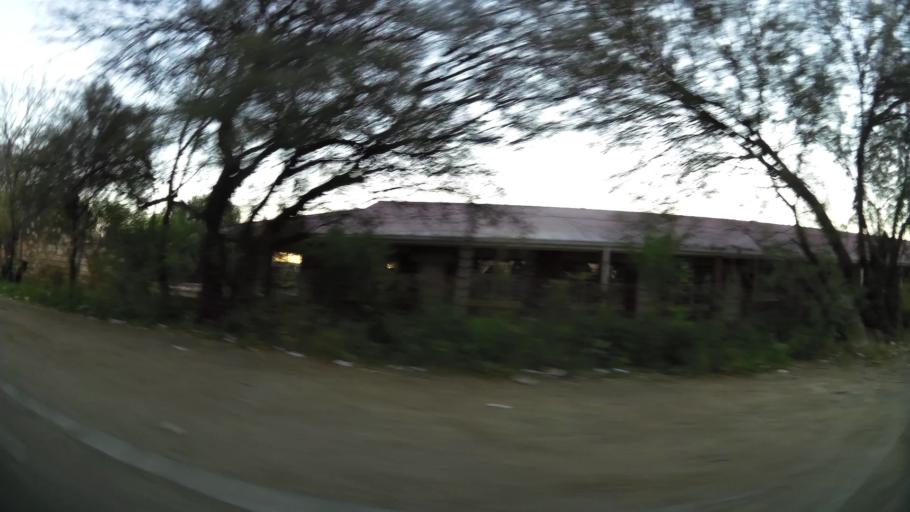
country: ZA
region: Northern Cape
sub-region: Frances Baard District Municipality
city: Kimberley
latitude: -28.7275
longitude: 24.7753
